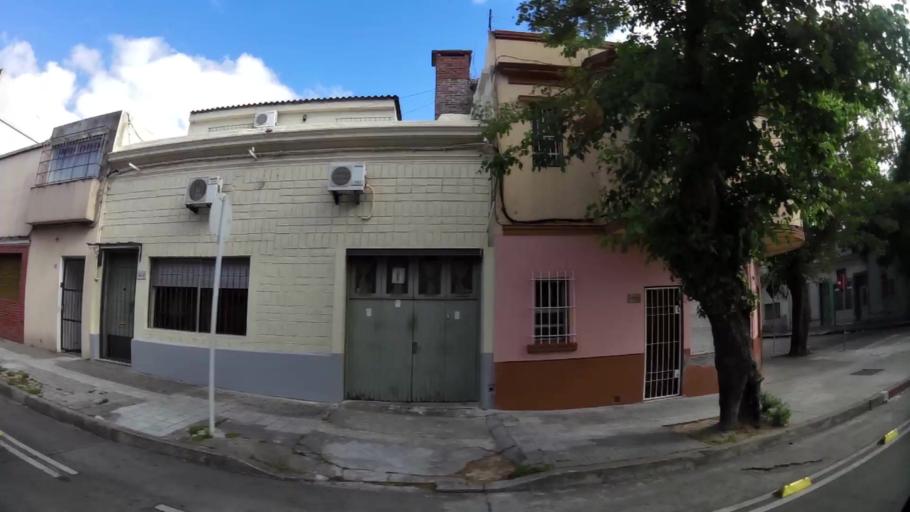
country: UY
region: Montevideo
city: Montevideo
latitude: -34.8889
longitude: -56.1671
